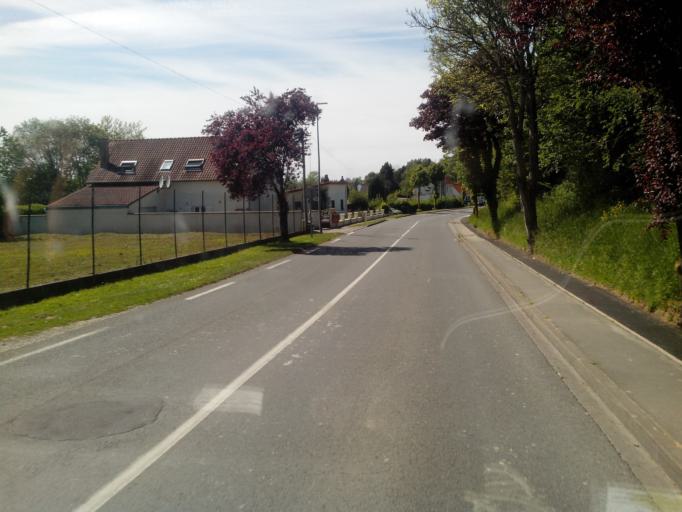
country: FR
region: Nord-Pas-de-Calais
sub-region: Departement du Pas-de-Calais
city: Montreuil
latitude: 50.4838
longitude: 1.7530
